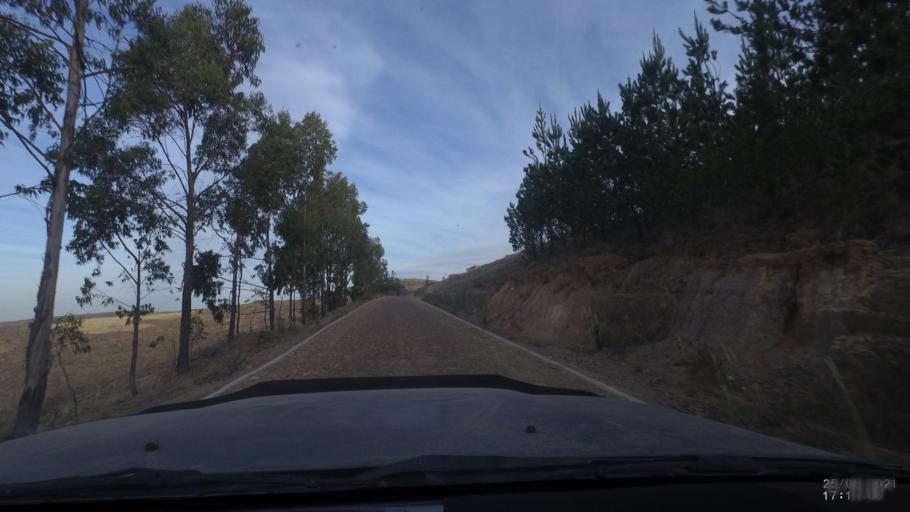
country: BO
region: Cochabamba
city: Arani
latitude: -17.8549
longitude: -65.6997
